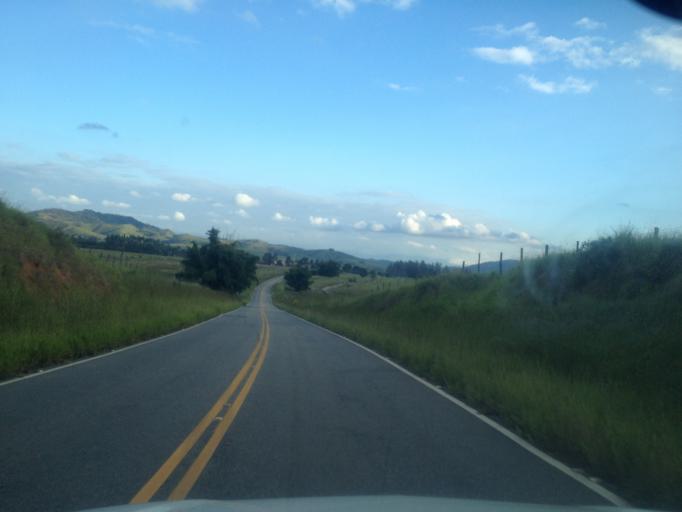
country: BR
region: Rio de Janeiro
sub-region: Quatis
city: Quatis
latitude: -22.3960
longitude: -44.2655
